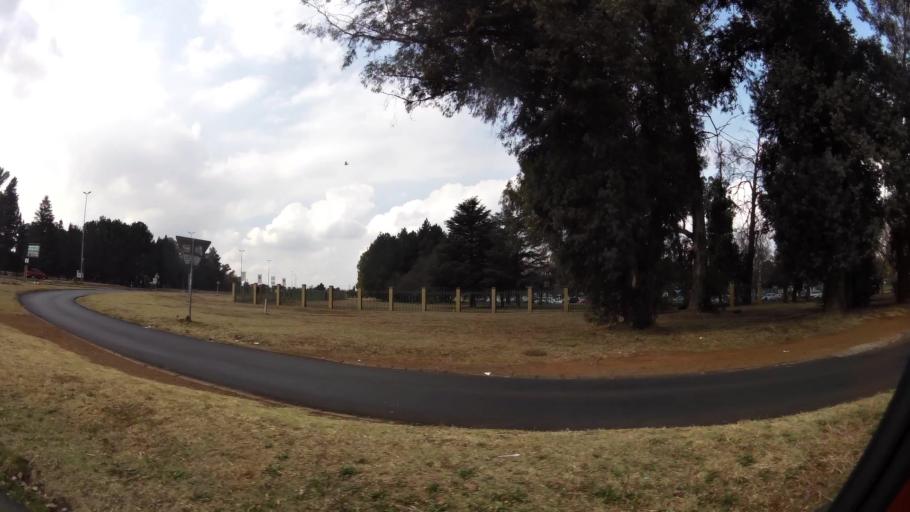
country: ZA
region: Gauteng
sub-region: Sedibeng District Municipality
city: Vanderbijlpark
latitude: -26.7084
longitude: 27.8602
